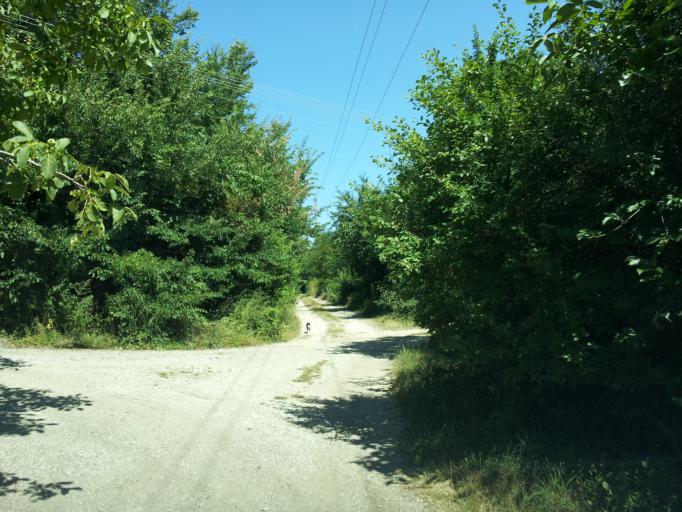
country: HU
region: Veszprem
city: Balatonkenese
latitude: 47.0223
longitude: 18.1627
